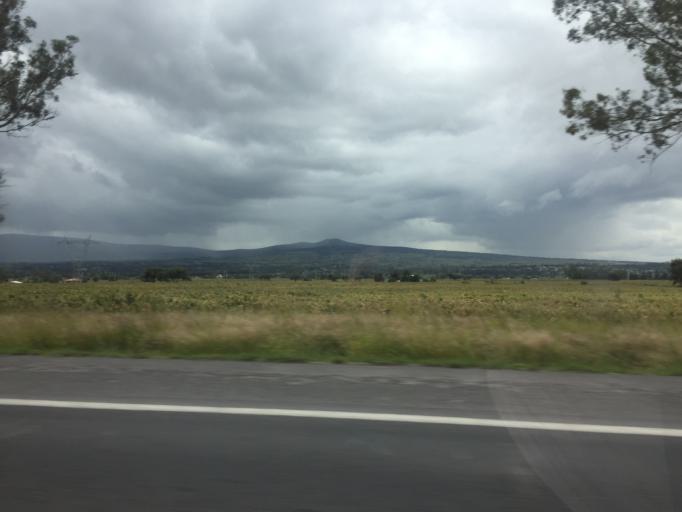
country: MX
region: Jalisco
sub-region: Zapotlanejo
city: La Mezquitera
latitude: 20.5661
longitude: -103.0779
